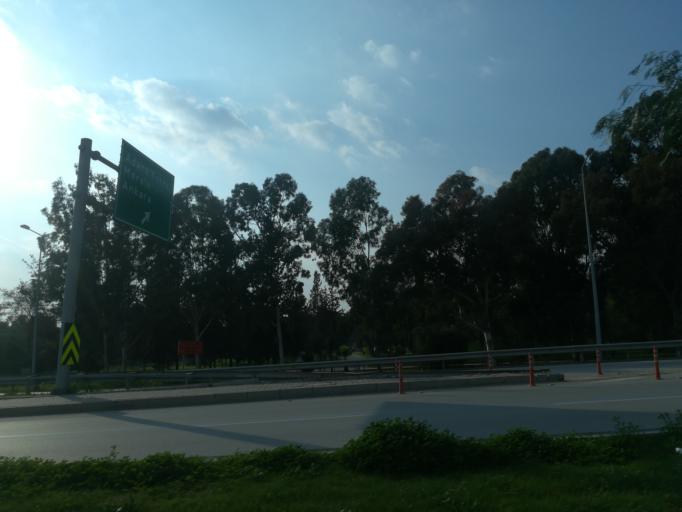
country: TR
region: Adana
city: Adana
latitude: 37.0266
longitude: 35.3444
